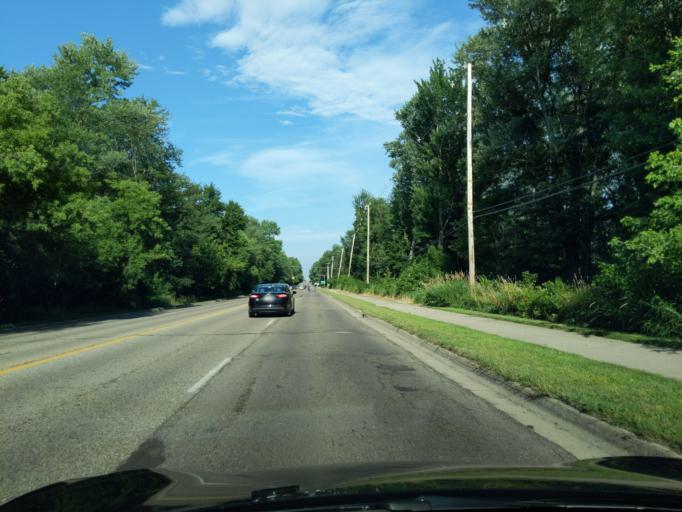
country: US
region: Michigan
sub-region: Ingham County
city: Okemos
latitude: 42.7469
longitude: -84.4508
